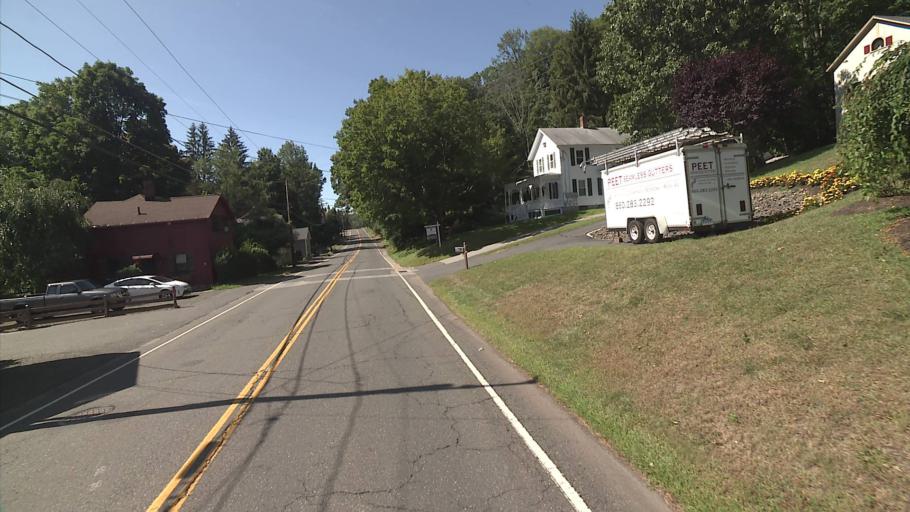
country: US
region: Connecticut
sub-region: Litchfield County
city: Thomaston
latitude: 41.6780
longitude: -73.0691
